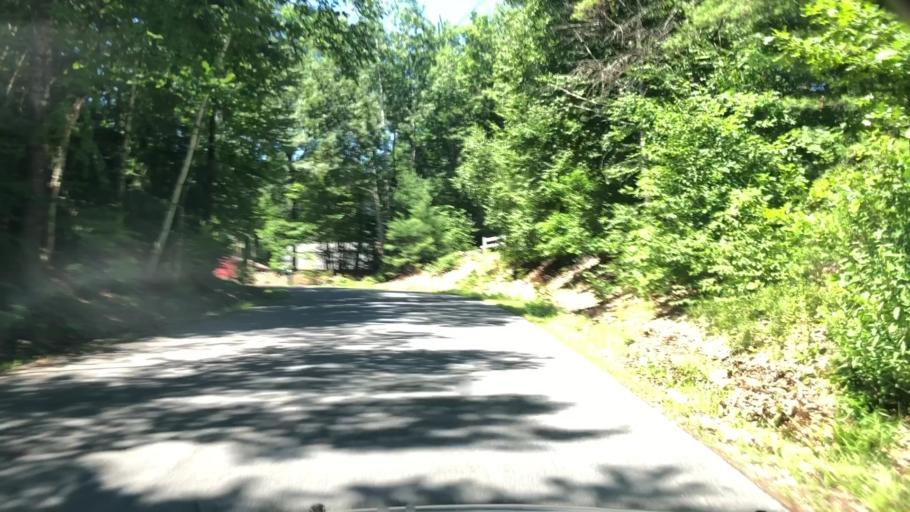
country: US
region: New Hampshire
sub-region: Hillsborough County
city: Milford
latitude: 42.8383
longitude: -71.5783
